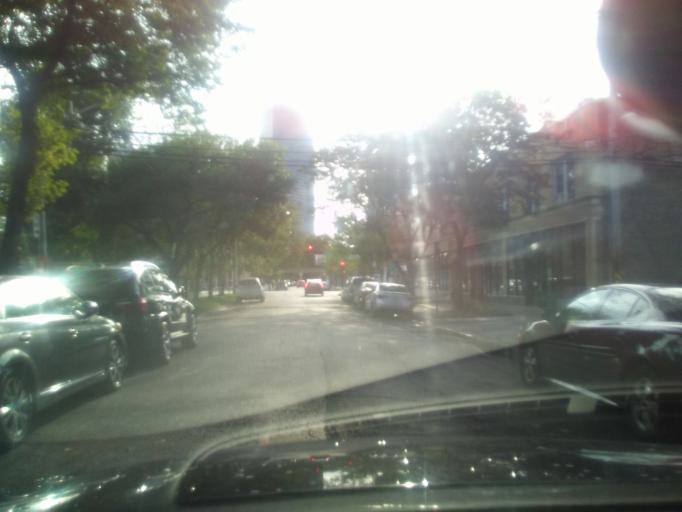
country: US
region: Illinois
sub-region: Cook County
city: Evanston
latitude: 41.9799
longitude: -87.6609
